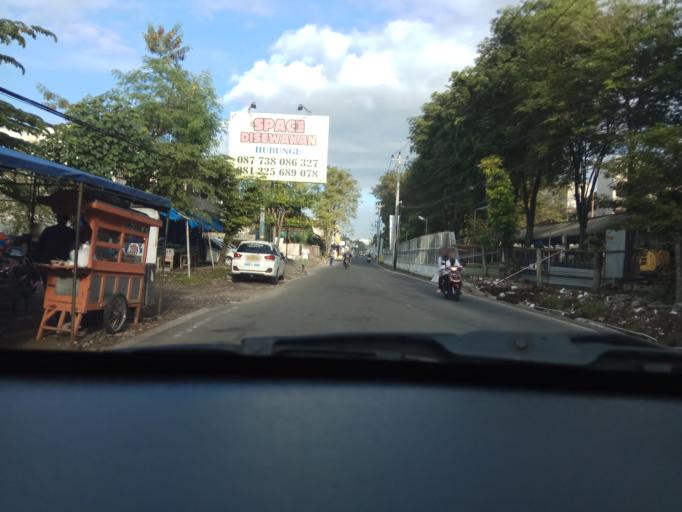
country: ID
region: Daerah Istimewa Yogyakarta
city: Depok
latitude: -7.7643
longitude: 110.4109
